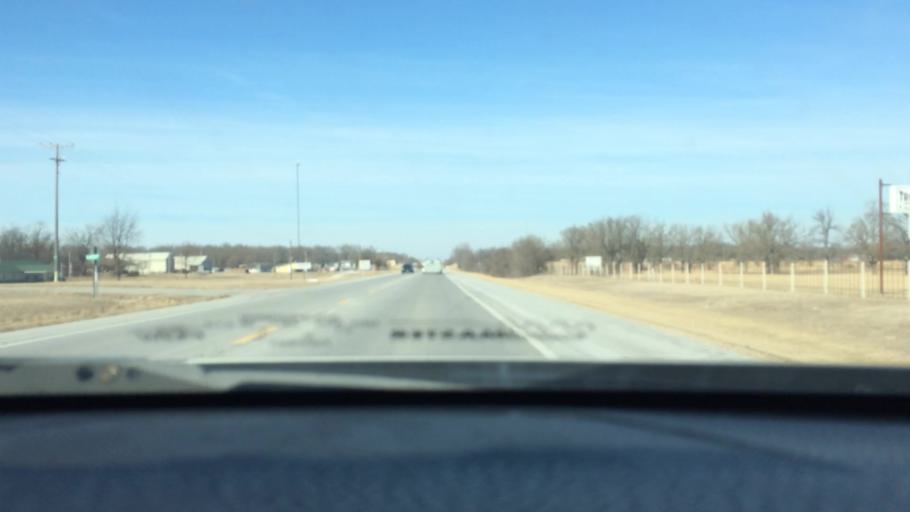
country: US
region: Missouri
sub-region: Newton County
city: Neosho
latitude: 36.8866
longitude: -94.3174
